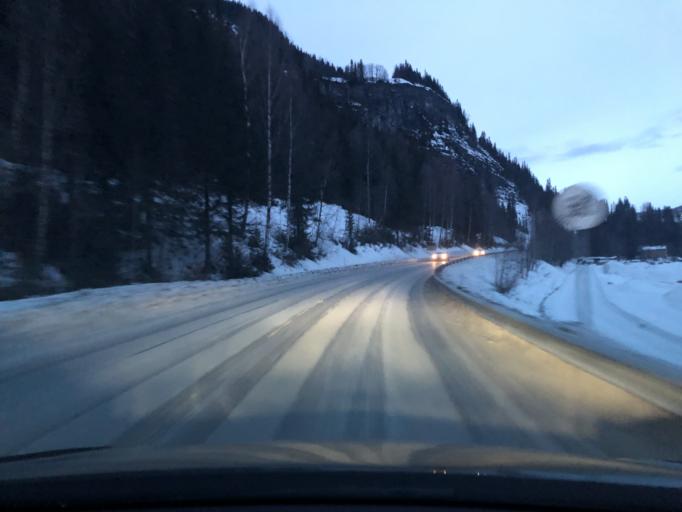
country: NO
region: Oppland
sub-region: Nord-Aurdal
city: Fagernes
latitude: 60.9984
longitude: 9.2111
